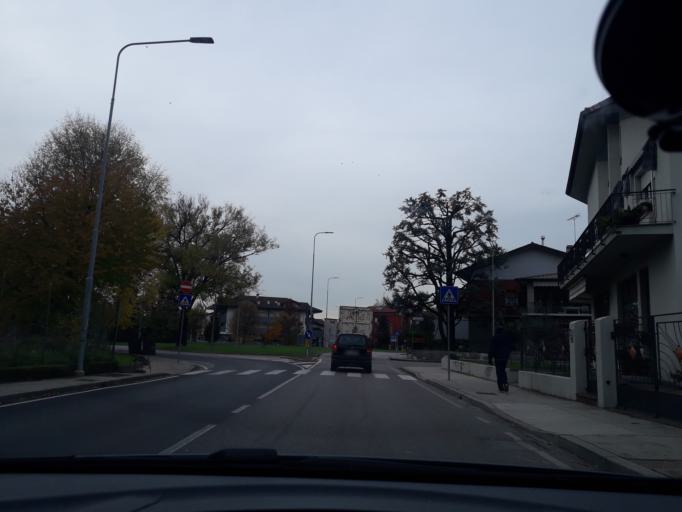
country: IT
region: Friuli Venezia Giulia
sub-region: Provincia di Udine
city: Feletto Umberto
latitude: 46.0825
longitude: 13.2244
